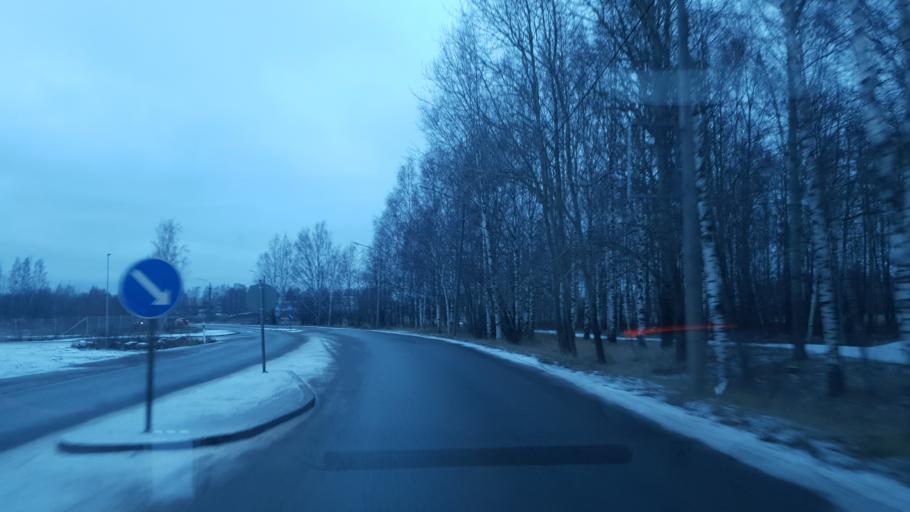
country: FI
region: Uusimaa
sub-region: Helsinki
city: Vantaa
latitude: 60.2433
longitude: 25.0258
